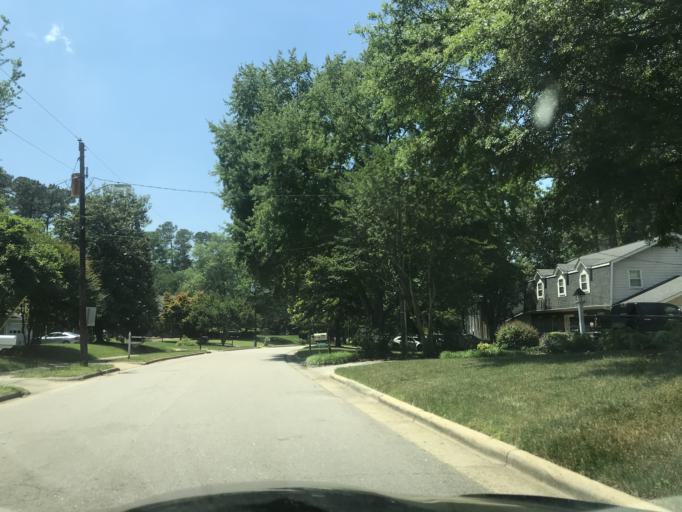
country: US
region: North Carolina
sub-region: Wake County
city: West Raleigh
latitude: 35.8491
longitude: -78.6168
